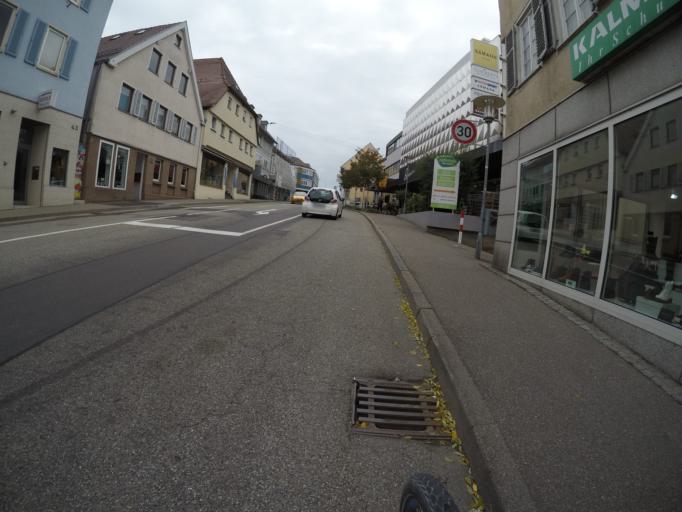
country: DE
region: Baden-Wuerttemberg
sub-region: Regierungsbezirk Stuttgart
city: Vaihingen an der Enz
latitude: 48.9305
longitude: 8.9595
